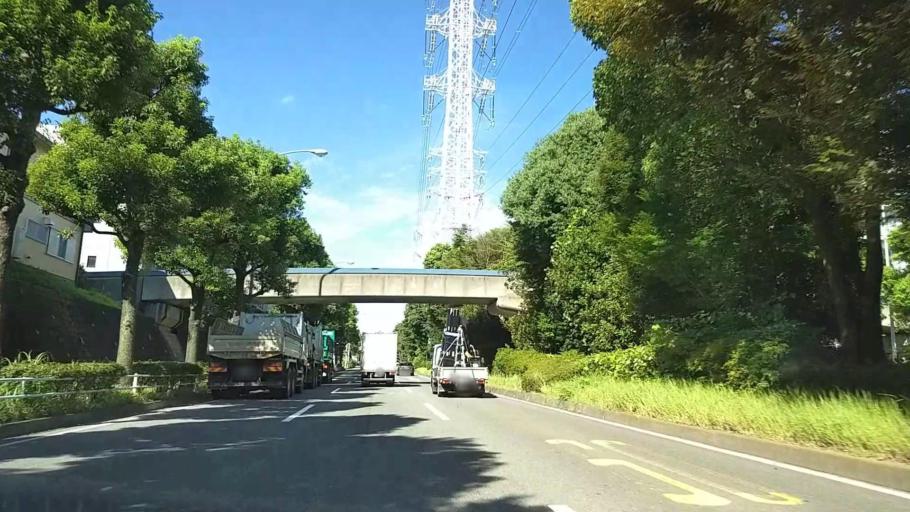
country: JP
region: Kanagawa
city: Yokohama
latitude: 35.5364
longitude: 139.5702
